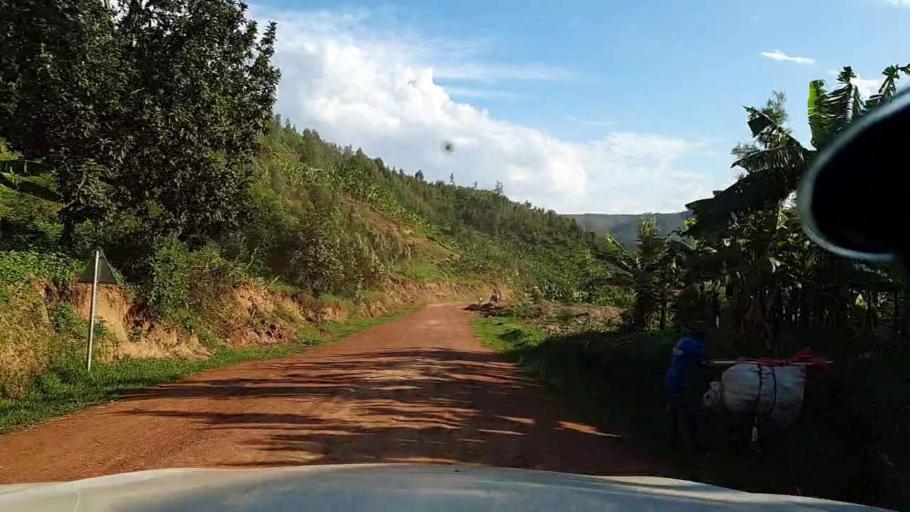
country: RW
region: Kigali
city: Kigali
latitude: -1.8658
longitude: 29.9314
